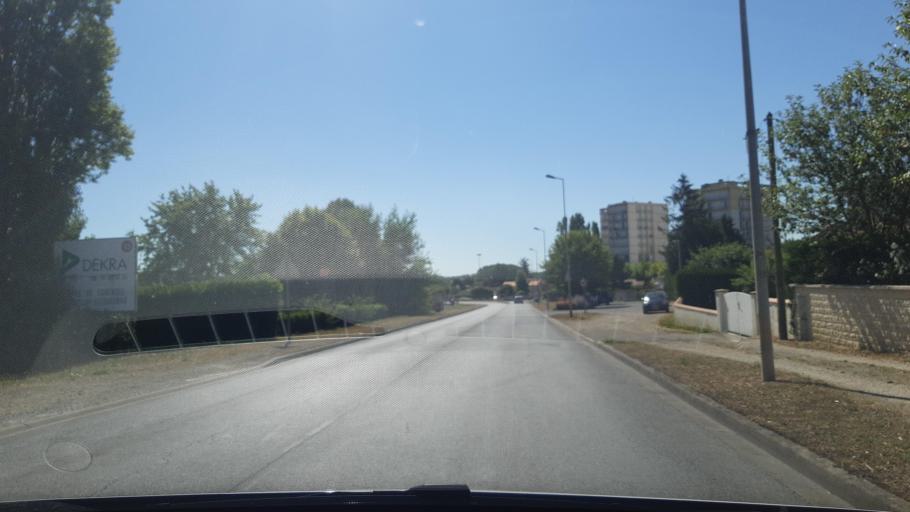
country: FR
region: Poitou-Charentes
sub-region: Departement des Deux-Sevres
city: Exireuil
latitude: 46.4198
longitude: -0.2061
